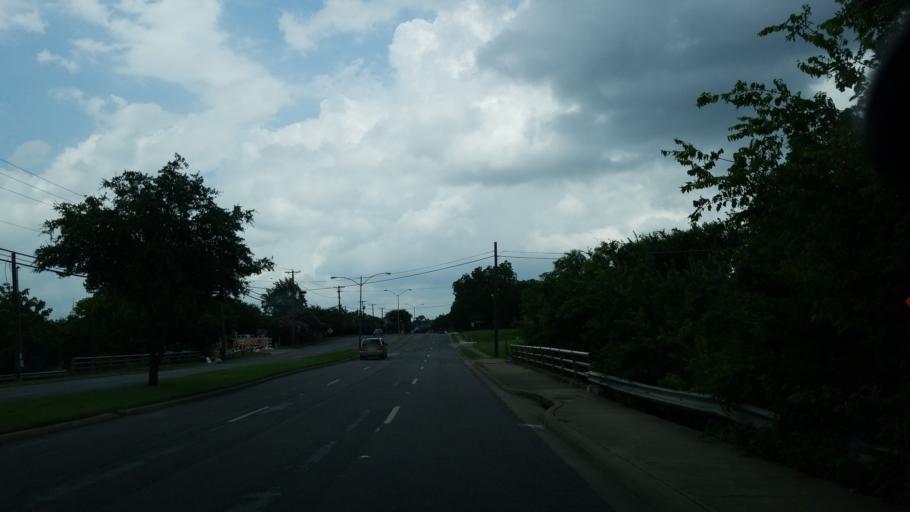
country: US
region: Texas
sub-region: Dallas County
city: Farmers Branch
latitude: 32.8807
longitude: -96.8616
